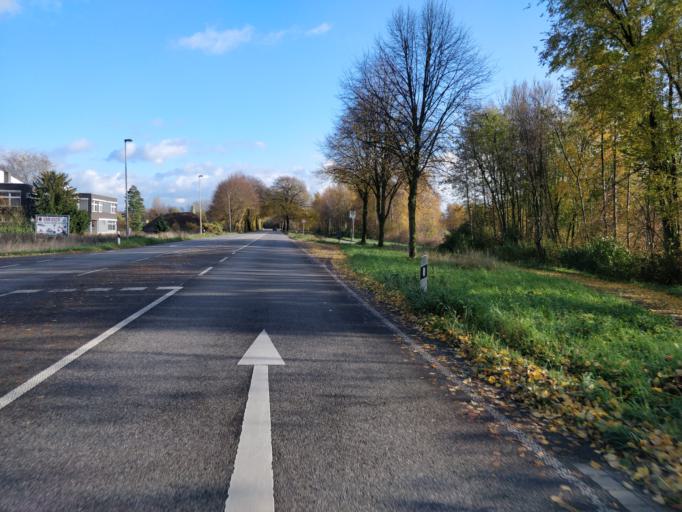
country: DE
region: North Rhine-Westphalia
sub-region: Regierungsbezirk Dusseldorf
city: Emmerich
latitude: 51.8304
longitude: 6.2775
